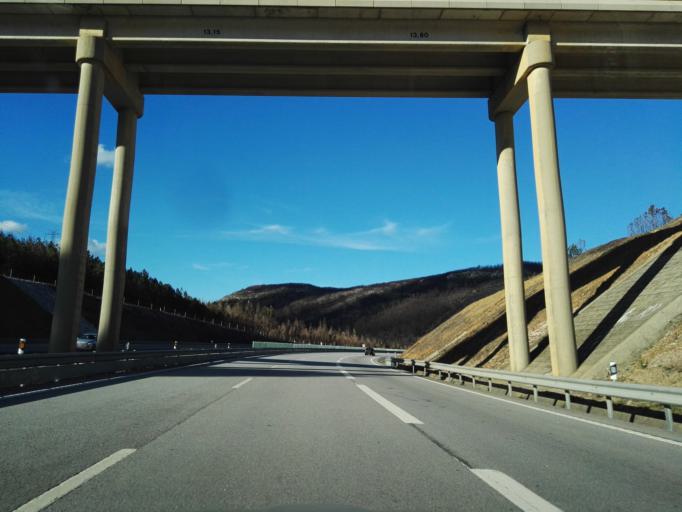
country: PT
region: Portalegre
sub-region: Nisa
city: Nisa
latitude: 39.6900
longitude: -7.7145
